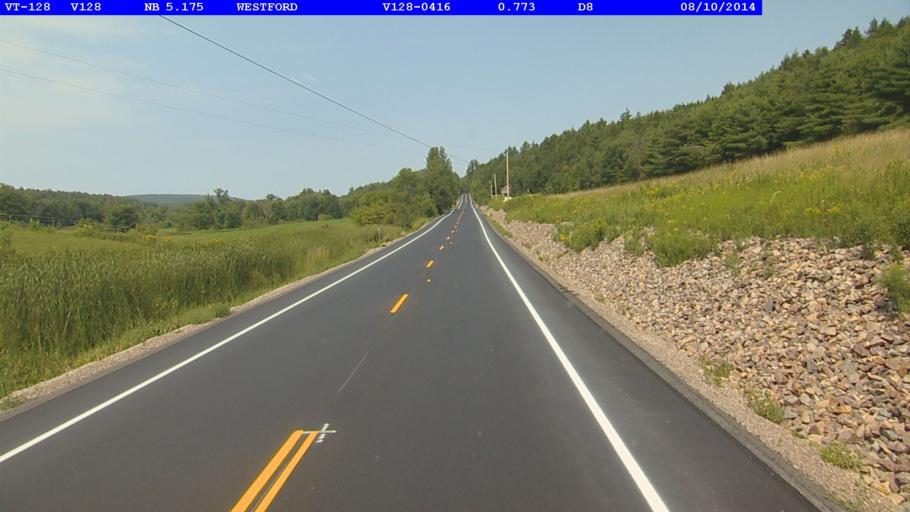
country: US
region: Vermont
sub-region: Chittenden County
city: Jericho
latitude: 44.5695
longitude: -73.0223
